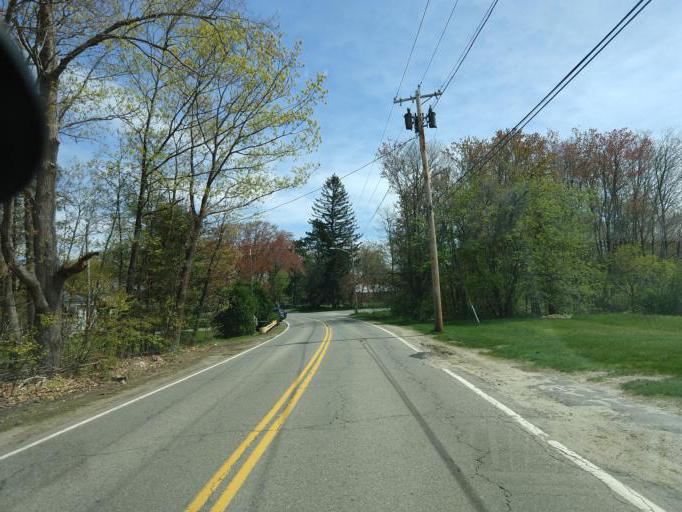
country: US
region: Massachusetts
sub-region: Essex County
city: Amesbury
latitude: 42.8587
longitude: -70.9066
